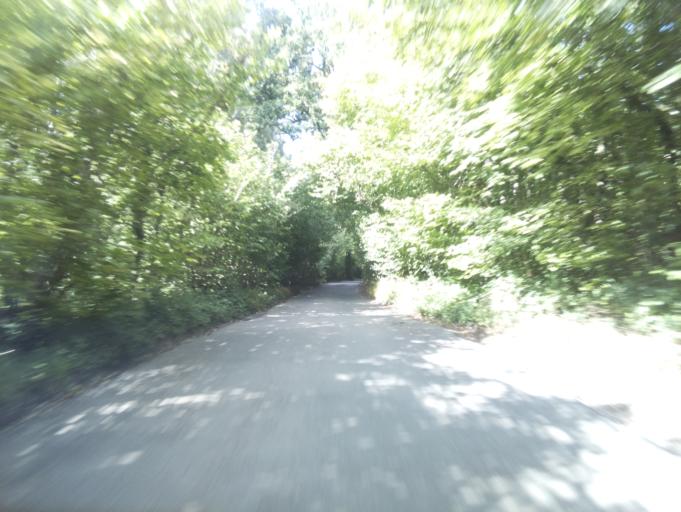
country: GB
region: England
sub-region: Hampshire
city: Chandlers Ford
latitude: 51.0627
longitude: -1.3806
